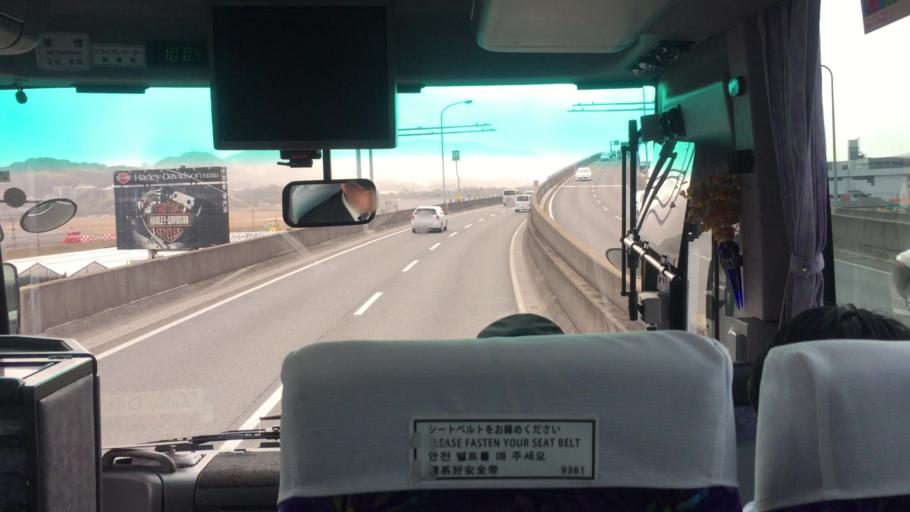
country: JP
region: Fukuoka
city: Fukuoka-shi
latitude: 33.5758
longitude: 130.4510
